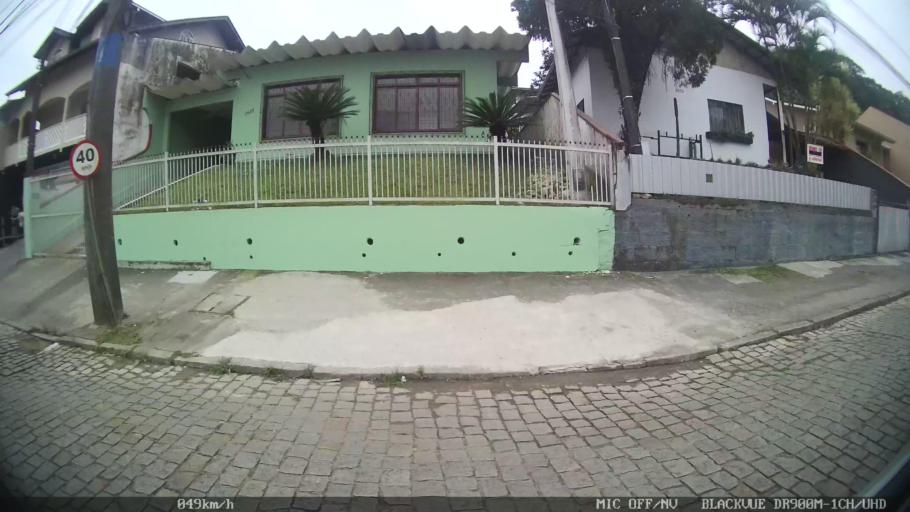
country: BR
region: Santa Catarina
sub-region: Joinville
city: Joinville
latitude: -26.3376
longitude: -48.8575
